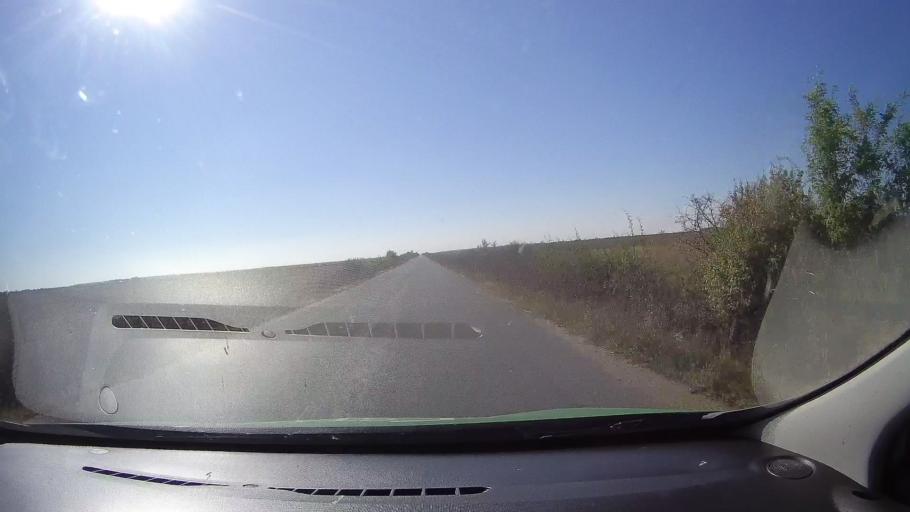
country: RO
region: Satu Mare
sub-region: Municipiul Satu Mare
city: Satmarel
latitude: 47.6987
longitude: 22.7686
